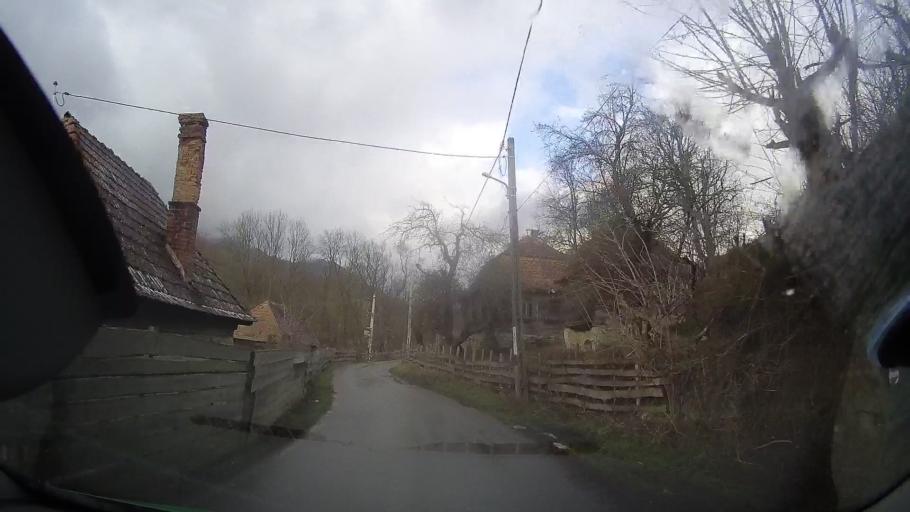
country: RO
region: Alba
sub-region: Comuna Ocolis
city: Ocolis
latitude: 46.4899
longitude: 23.4586
